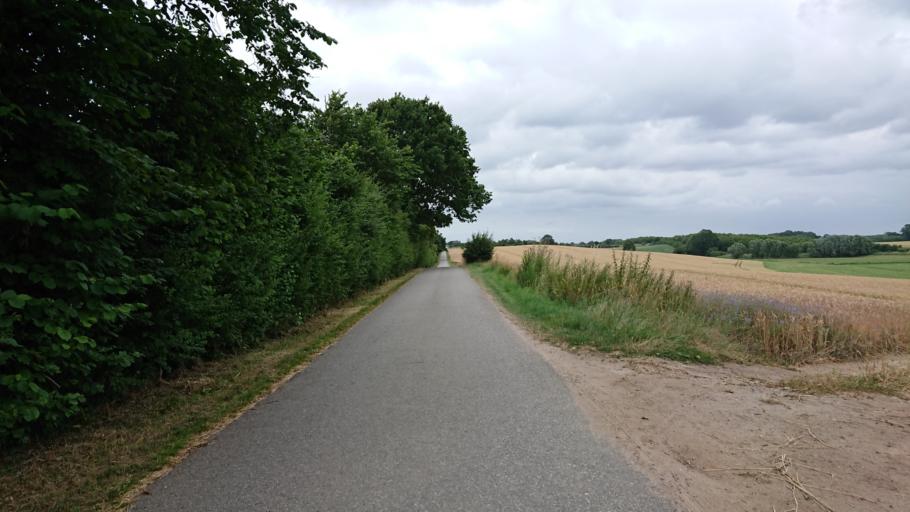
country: DE
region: Schleswig-Holstein
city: Gross Sarau
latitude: 53.7867
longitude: 10.7285
